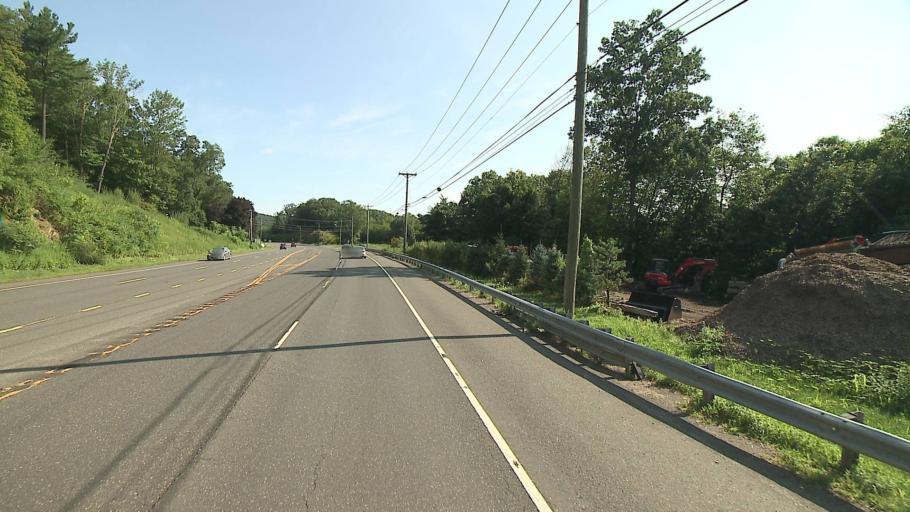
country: US
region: Connecticut
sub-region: Fairfield County
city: Danbury
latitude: 41.3370
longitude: -73.4707
